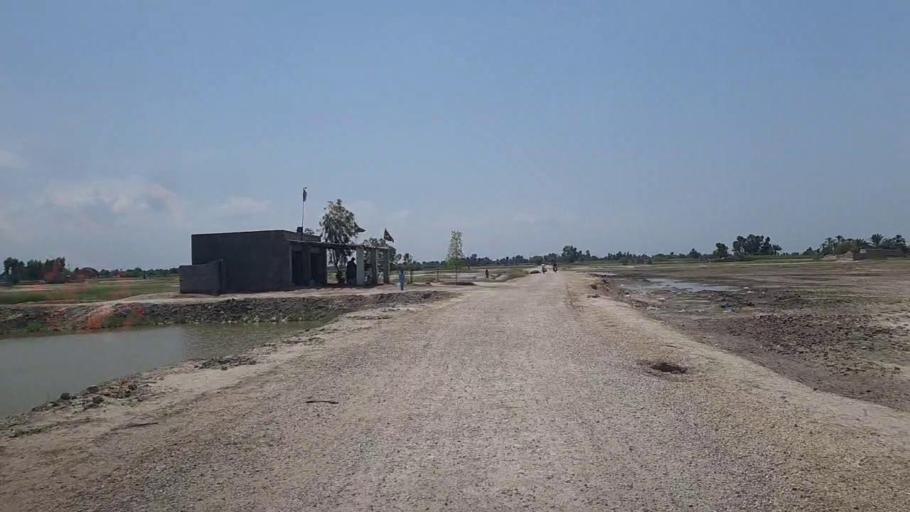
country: PK
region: Sindh
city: Ubauro
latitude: 28.1606
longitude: 69.7645
